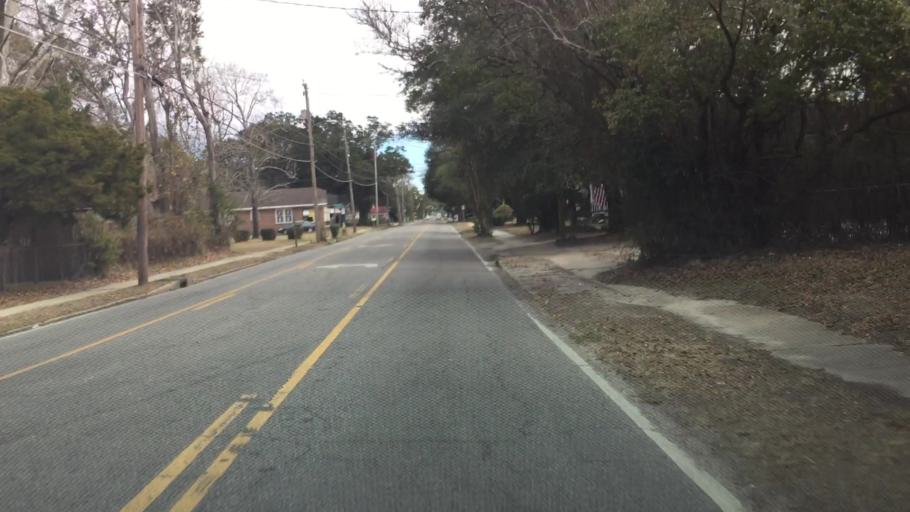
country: US
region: Alabama
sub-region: Mobile County
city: Mobile
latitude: 30.6744
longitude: -88.0727
